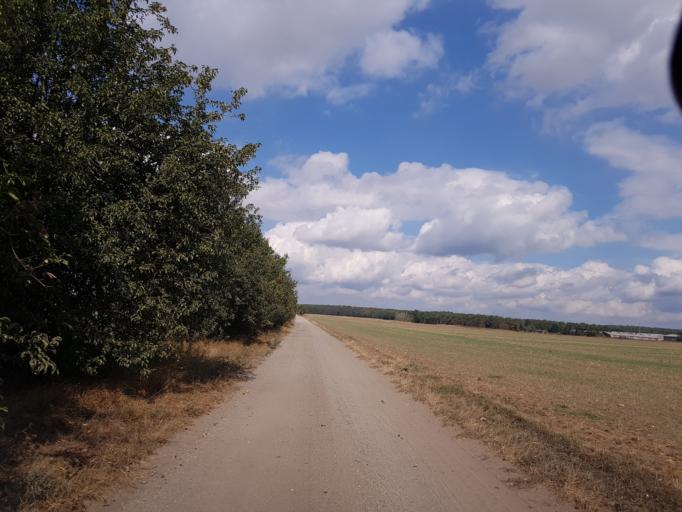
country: DE
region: Brandenburg
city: Finsterwalde
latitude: 51.6252
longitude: 13.7553
